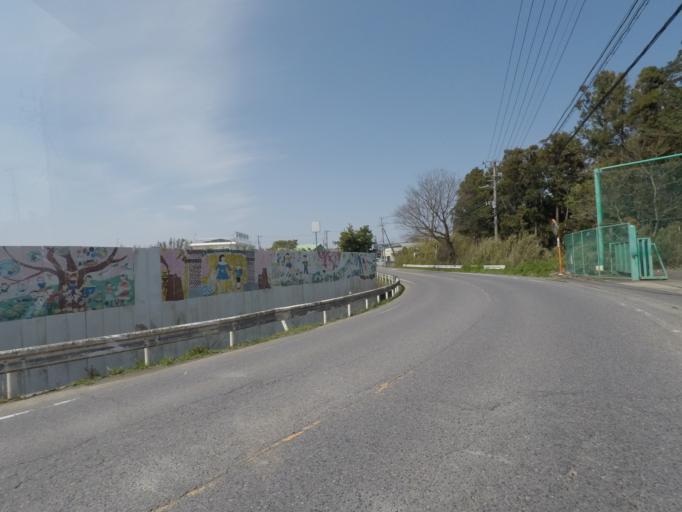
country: JP
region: Chiba
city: Narita
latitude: 35.7836
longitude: 140.3405
